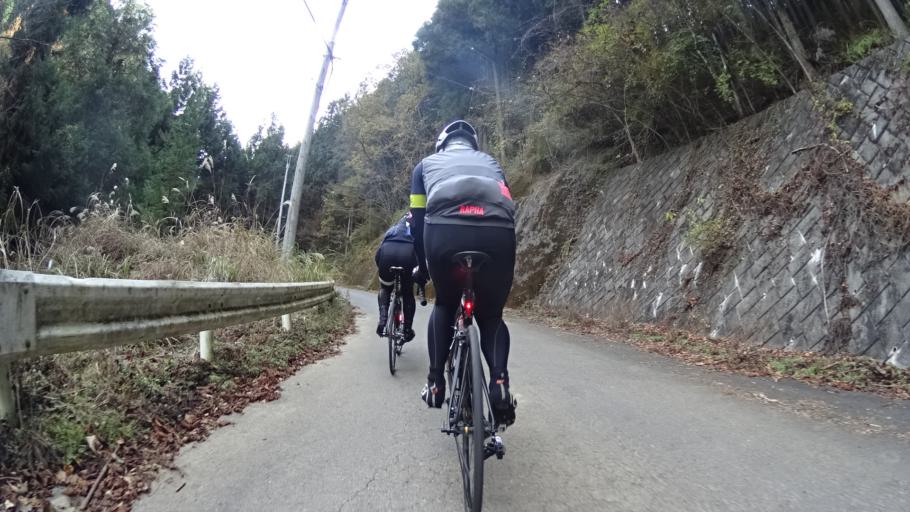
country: JP
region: Saitama
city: Chichibu
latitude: 35.9162
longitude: 139.1778
